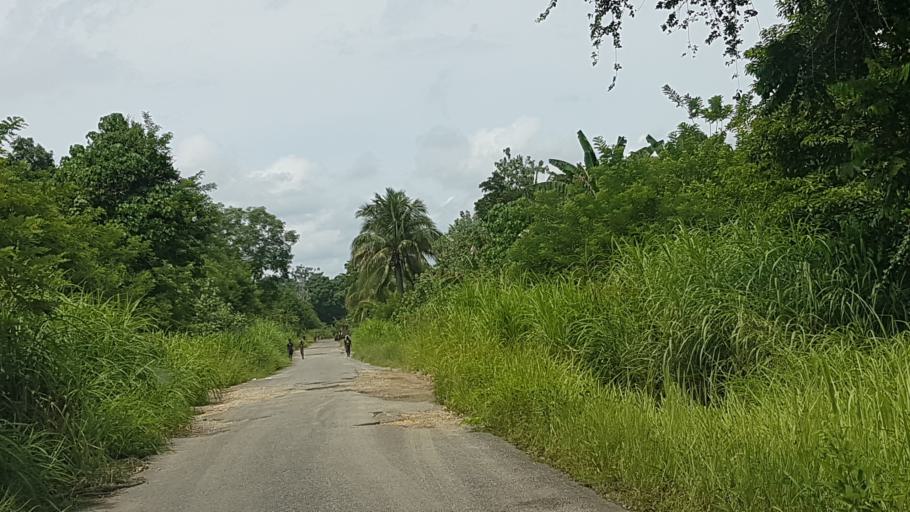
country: PG
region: Madang
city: Madang
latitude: -4.5906
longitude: 145.5342
